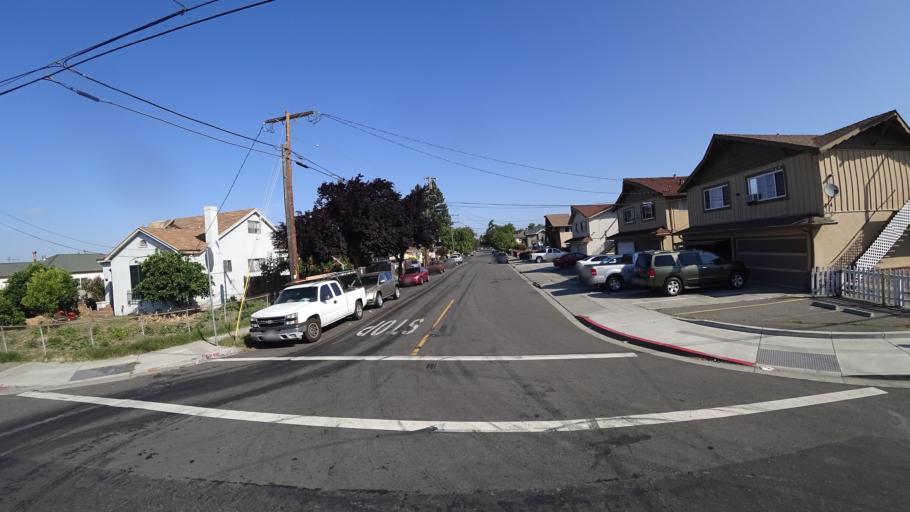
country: US
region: California
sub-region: Alameda County
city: Hayward
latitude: 37.6541
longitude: -122.0781
